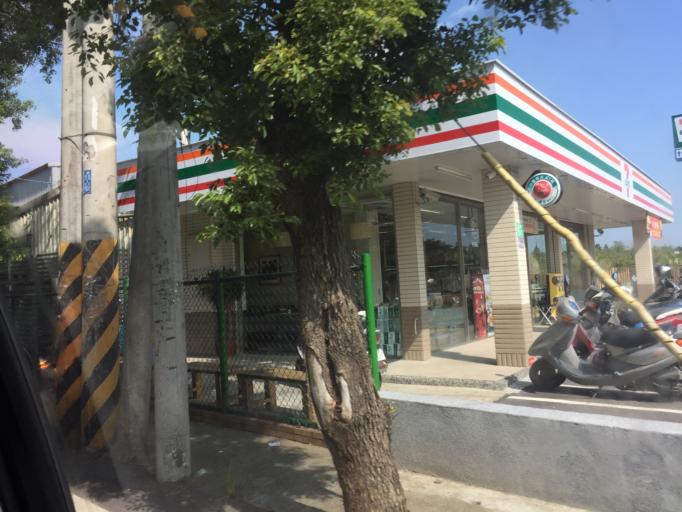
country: TW
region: Taiwan
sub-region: Taoyuan
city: Taoyuan
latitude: 24.9371
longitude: 121.3060
